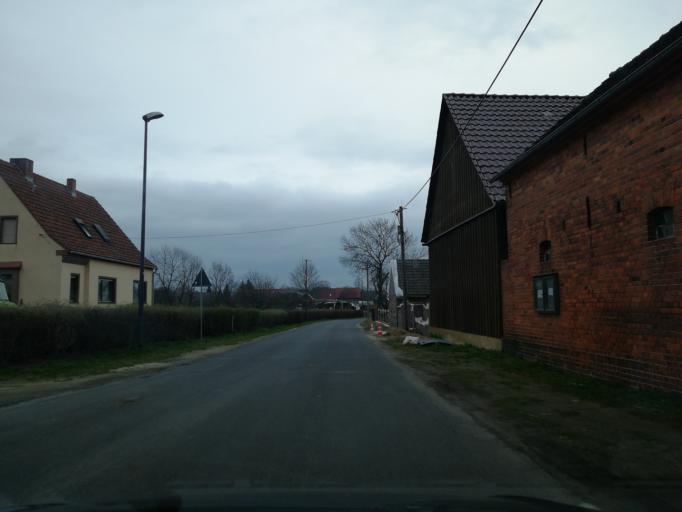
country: DE
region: Brandenburg
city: Vetschau
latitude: 51.7484
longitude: 14.0288
